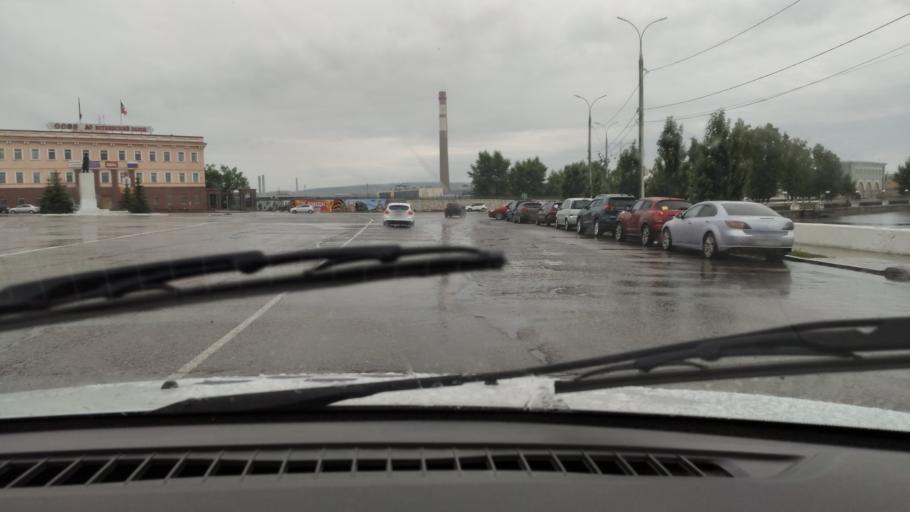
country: RU
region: Udmurtiya
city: Votkinsk
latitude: 57.0530
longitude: 53.9852
